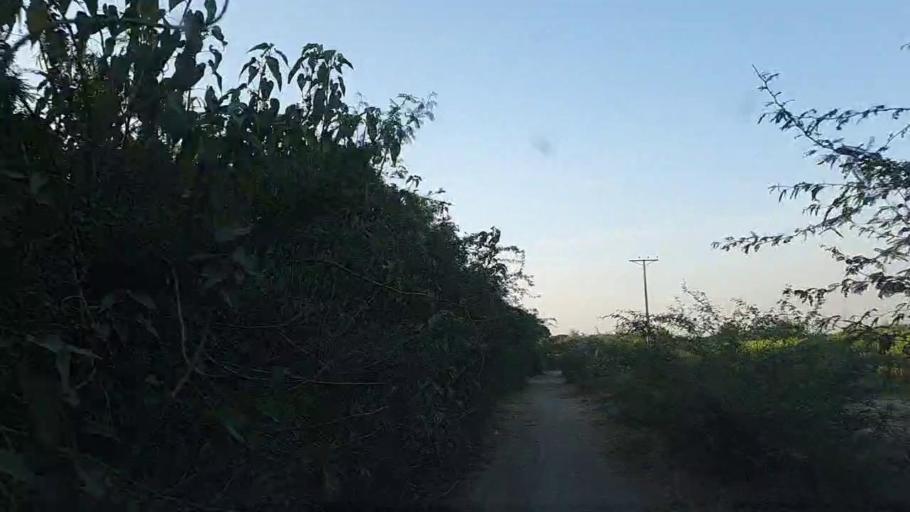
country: PK
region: Sindh
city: Mirpur Batoro
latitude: 24.7272
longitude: 68.2125
